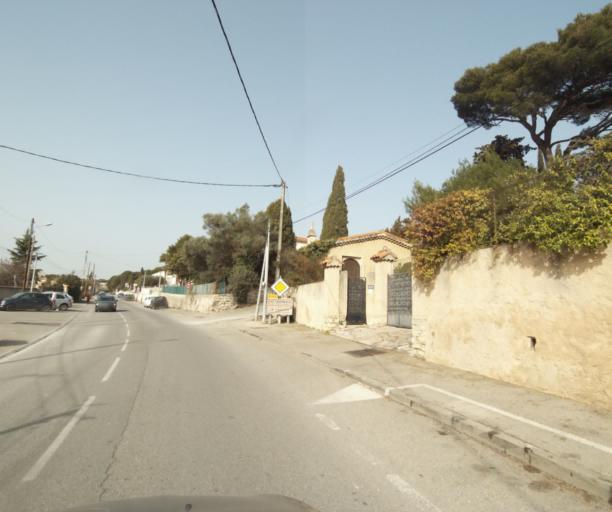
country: FR
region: Provence-Alpes-Cote d'Azur
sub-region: Departement des Bouches-du-Rhone
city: Marseille 15
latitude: 43.3870
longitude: 5.3461
